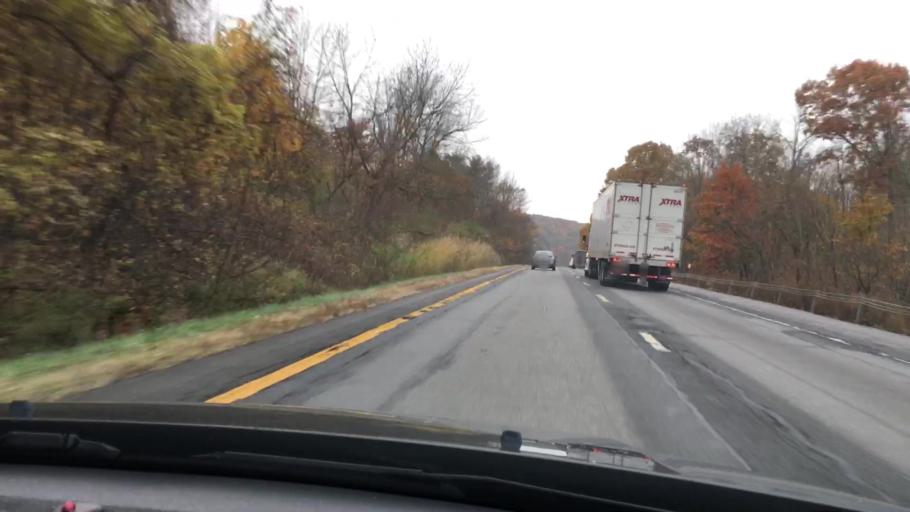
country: US
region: New York
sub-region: Putnam County
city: Lake Carmel
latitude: 41.4863
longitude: -73.6587
